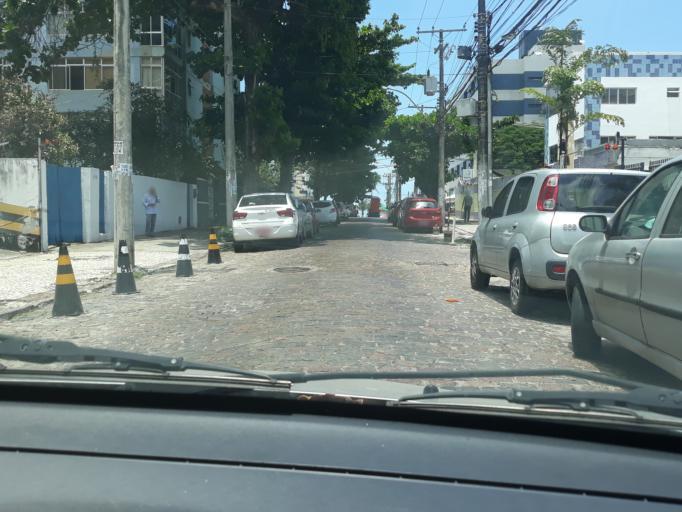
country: BR
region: Bahia
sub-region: Salvador
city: Salvador
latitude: -13.0089
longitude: -38.5082
